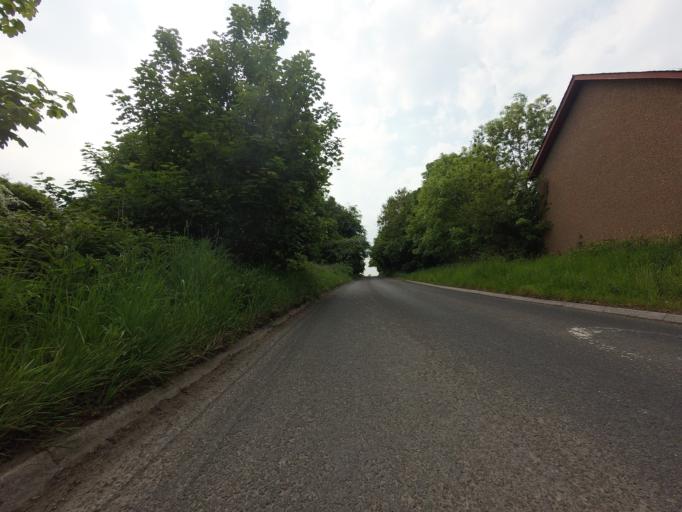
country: GB
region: Scotland
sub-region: Fife
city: Inverkeithing
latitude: 56.0465
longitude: -3.4043
